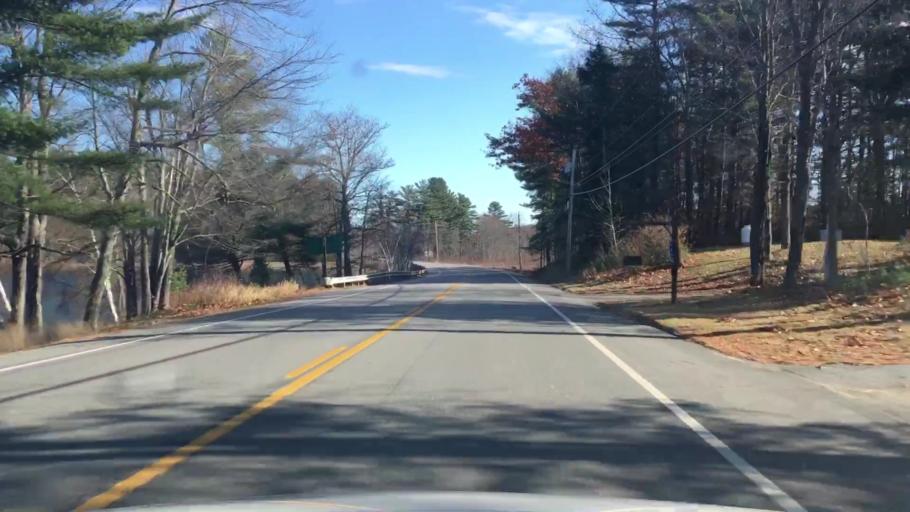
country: US
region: Maine
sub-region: Kennebec County
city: Windsor
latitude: 44.2501
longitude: -69.5358
